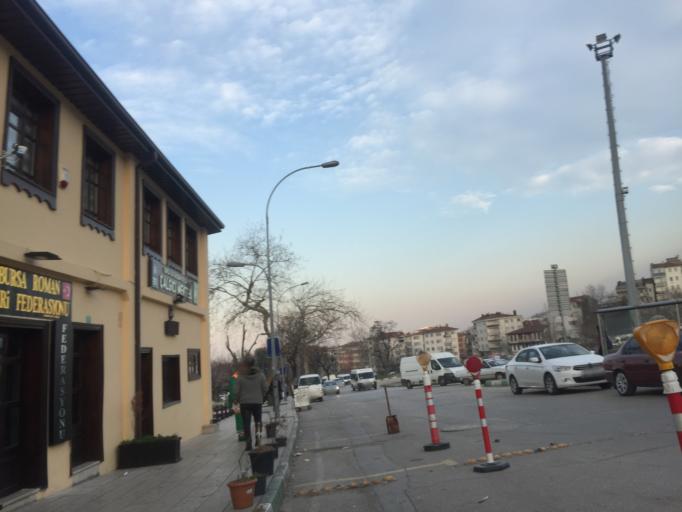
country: TR
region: Bursa
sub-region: Osmangazi
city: Bursa
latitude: 40.1848
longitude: 29.0731
